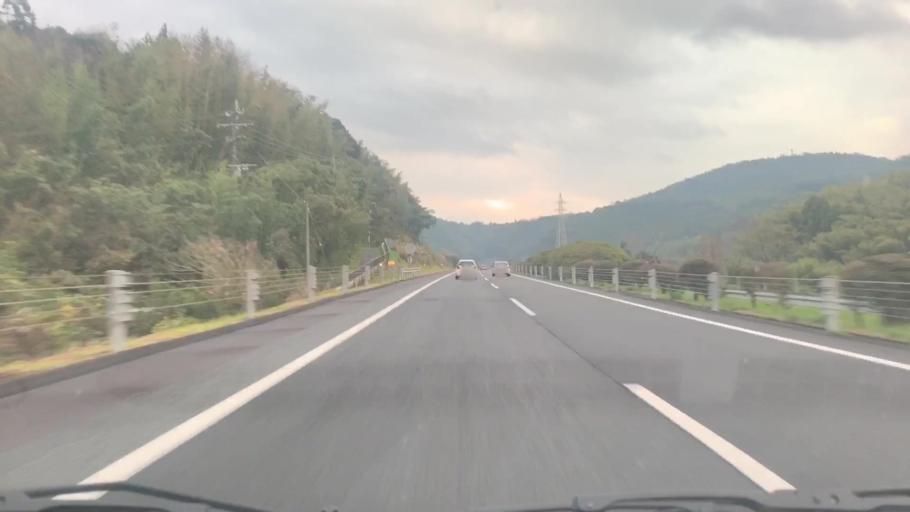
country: JP
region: Nagasaki
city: Omura
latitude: 32.8824
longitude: 129.9957
